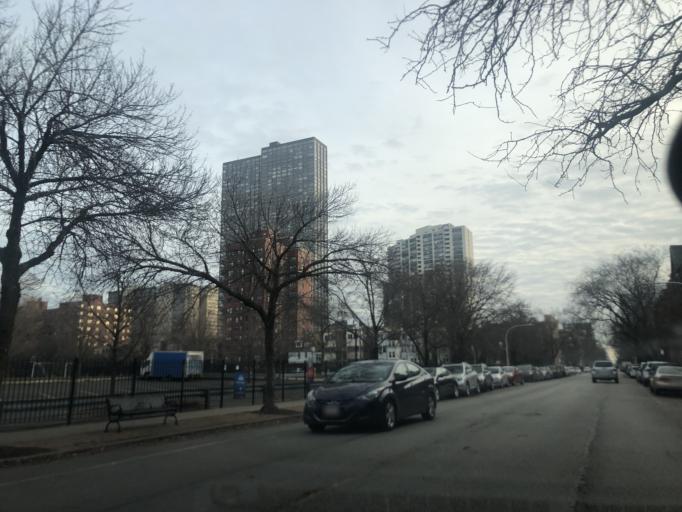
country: US
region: Illinois
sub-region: Cook County
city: Evanston
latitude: 41.9573
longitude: -87.6499
